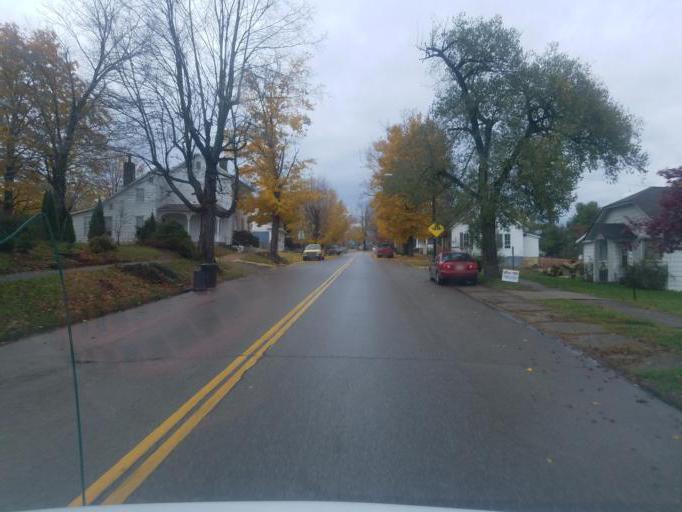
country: US
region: Ohio
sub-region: Morgan County
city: McConnelsville
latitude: 39.4907
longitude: -81.8652
